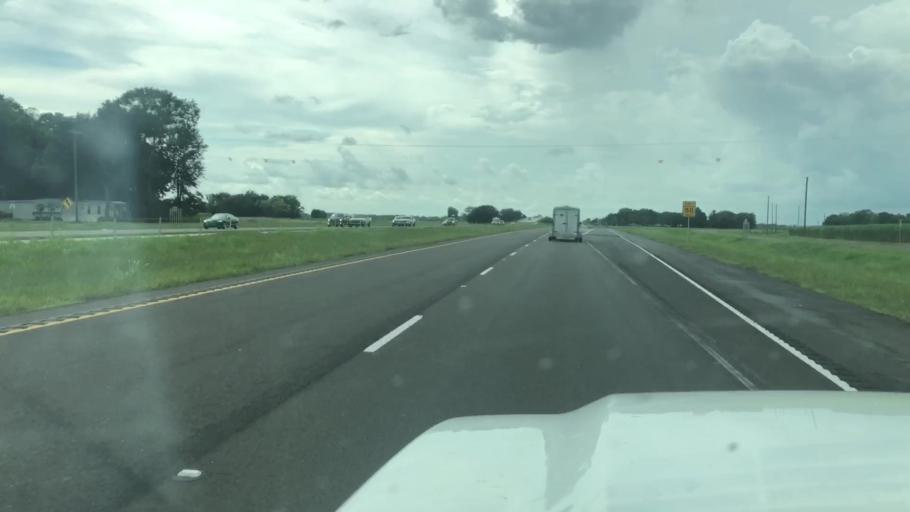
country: US
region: Louisiana
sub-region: Iberia Parish
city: Jeanerette
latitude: 29.8629
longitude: -91.6260
